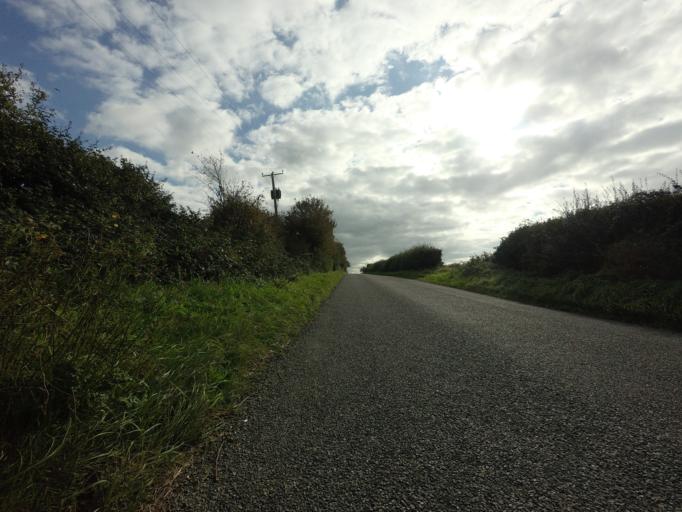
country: GB
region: England
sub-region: Norfolk
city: Snettisham
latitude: 52.9038
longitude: 0.5436
